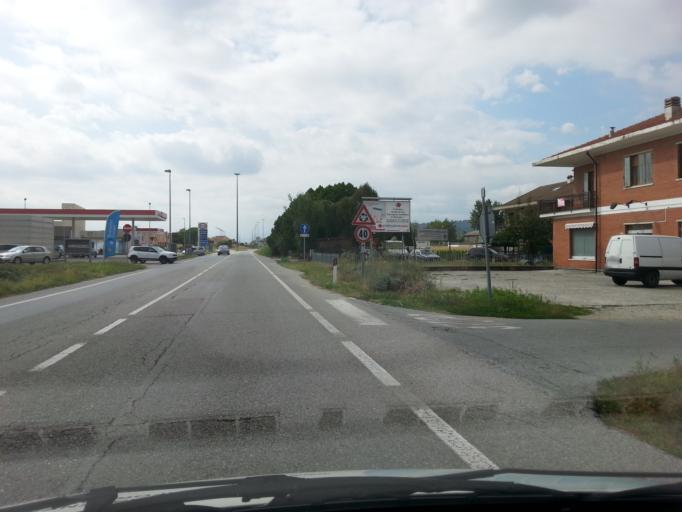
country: IT
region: Piedmont
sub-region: Provincia di Torino
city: Frossasco
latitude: 44.9301
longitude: 7.3695
